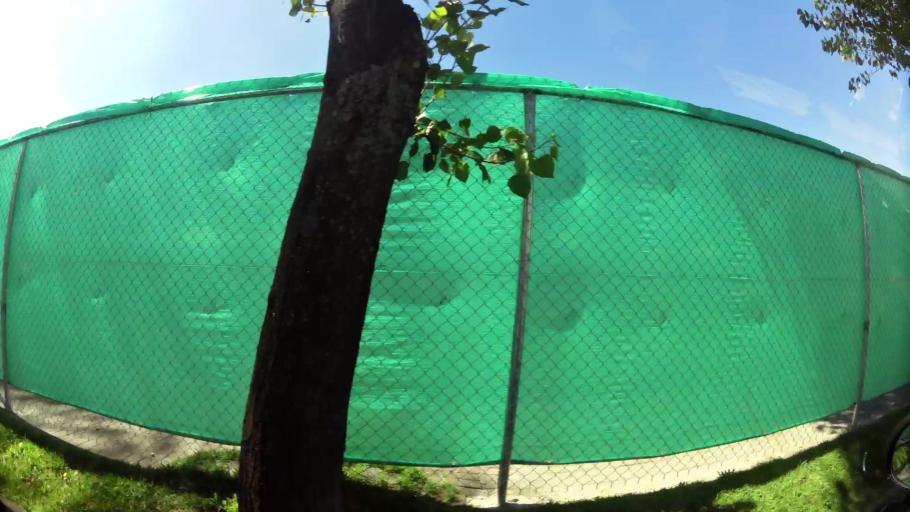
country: EC
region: Pichincha
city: Quito
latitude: -0.2576
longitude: -78.5336
